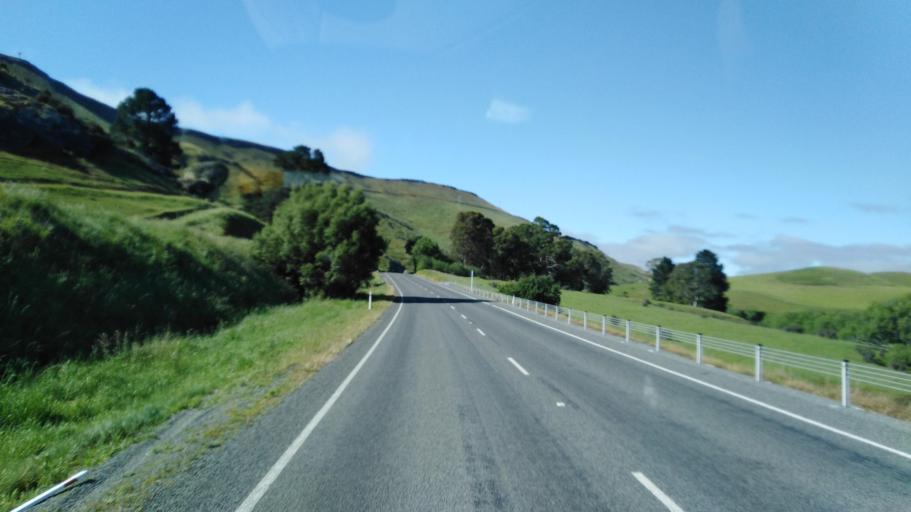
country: NZ
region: Canterbury
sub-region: Hurunui District
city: Amberley
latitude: -42.9907
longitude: 172.7202
